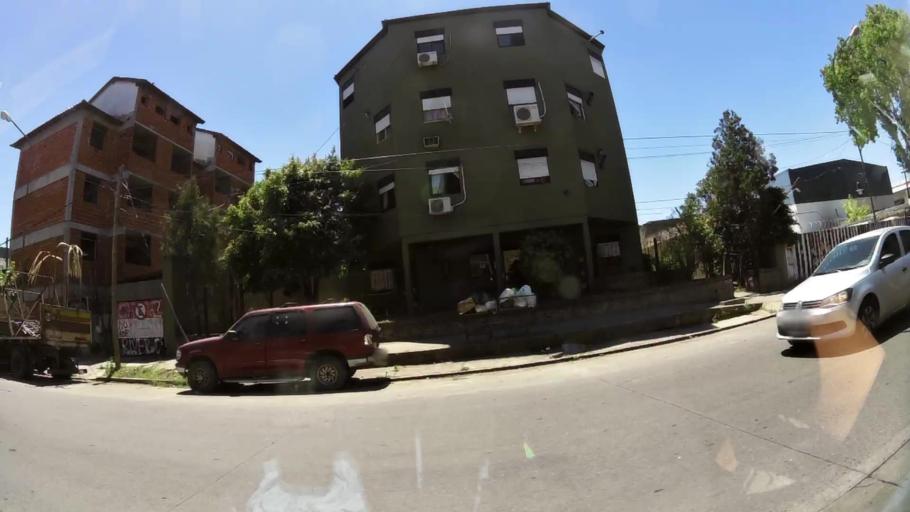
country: AR
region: Buenos Aires
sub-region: Partido de General San Martin
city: General San Martin
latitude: -34.5543
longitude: -58.5218
